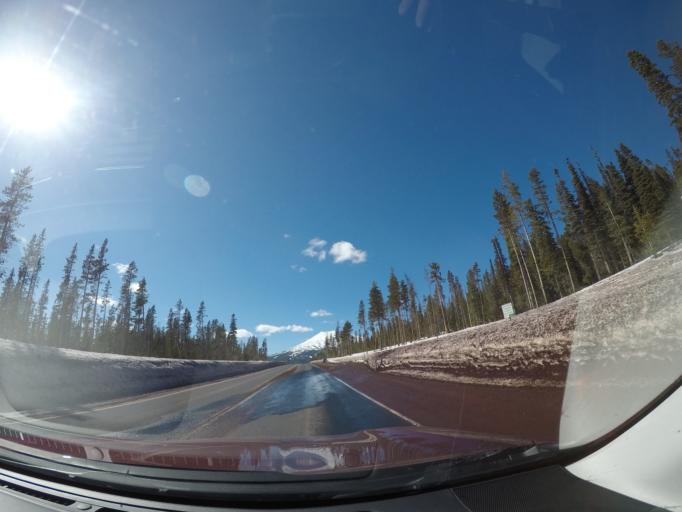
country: US
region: Oregon
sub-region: Deschutes County
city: Sunriver
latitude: 43.9838
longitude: -121.6049
